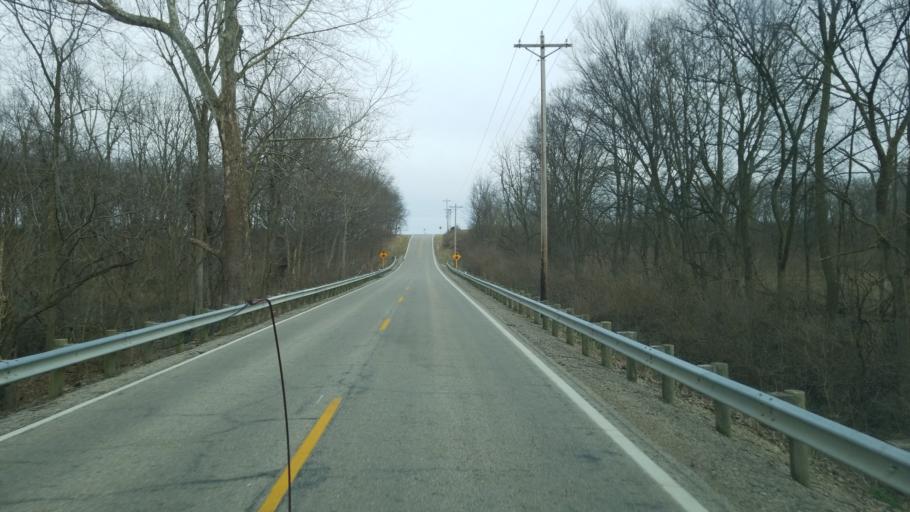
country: US
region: Ohio
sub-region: Pickaway County
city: Williamsport
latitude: 39.5500
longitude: -83.1155
